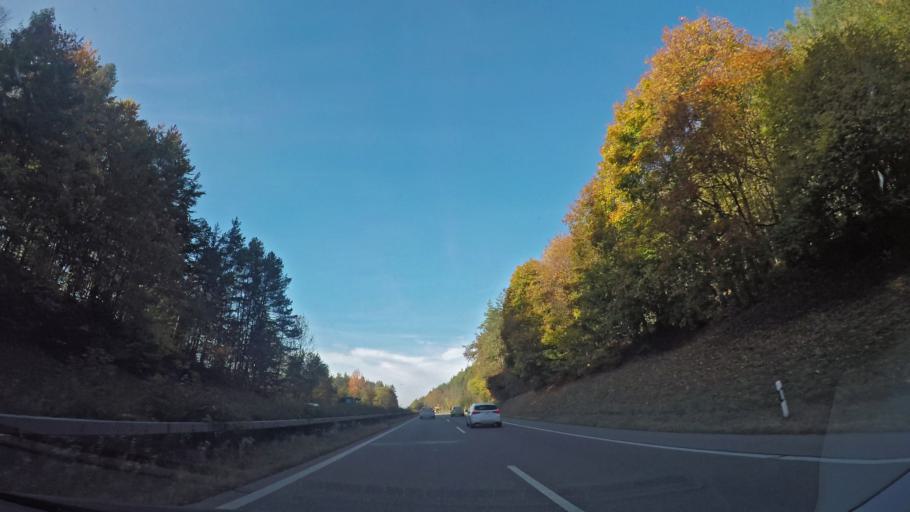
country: CH
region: Bern
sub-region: Thun District
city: Thun
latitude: 46.7225
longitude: 7.6085
